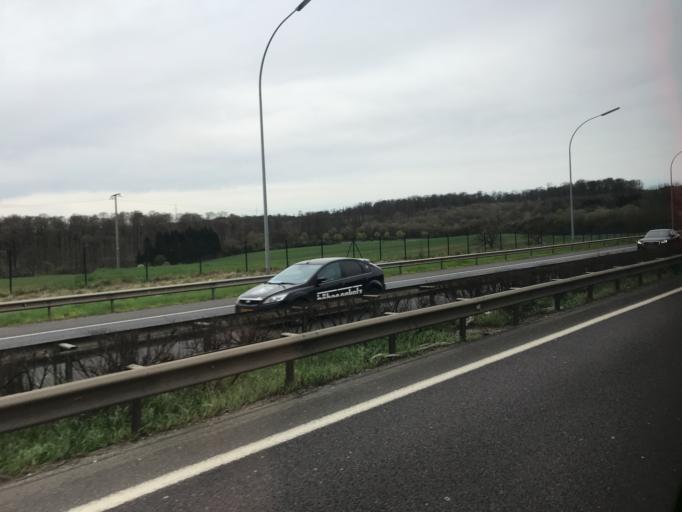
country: LU
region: Luxembourg
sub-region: Canton d'Esch-sur-Alzette
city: Leudelange
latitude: 49.5614
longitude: 6.0702
